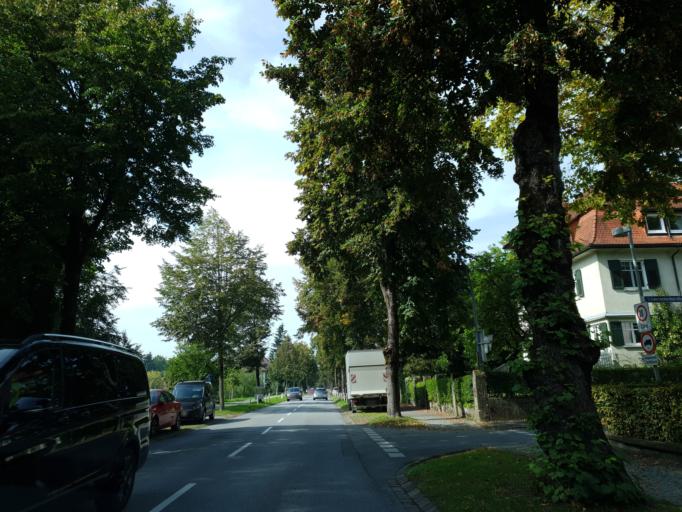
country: AT
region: Vorarlberg
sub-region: Politischer Bezirk Bregenz
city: Bregenz
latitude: 47.4942
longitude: 9.7397
